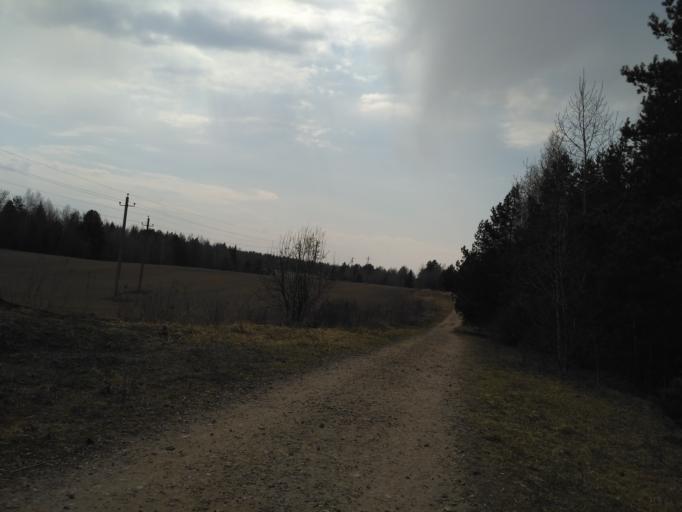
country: BY
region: Minsk
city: Zamostochcha
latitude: 53.8812
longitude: 27.9109
